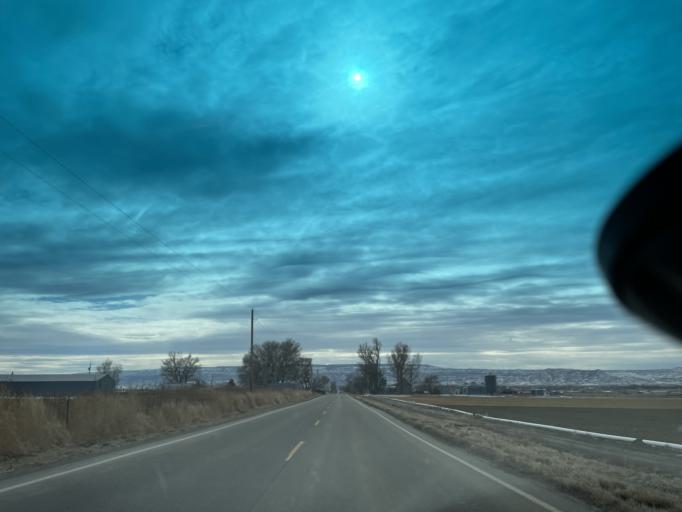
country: US
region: Colorado
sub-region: Mesa County
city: Loma
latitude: 39.2580
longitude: -108.8128
